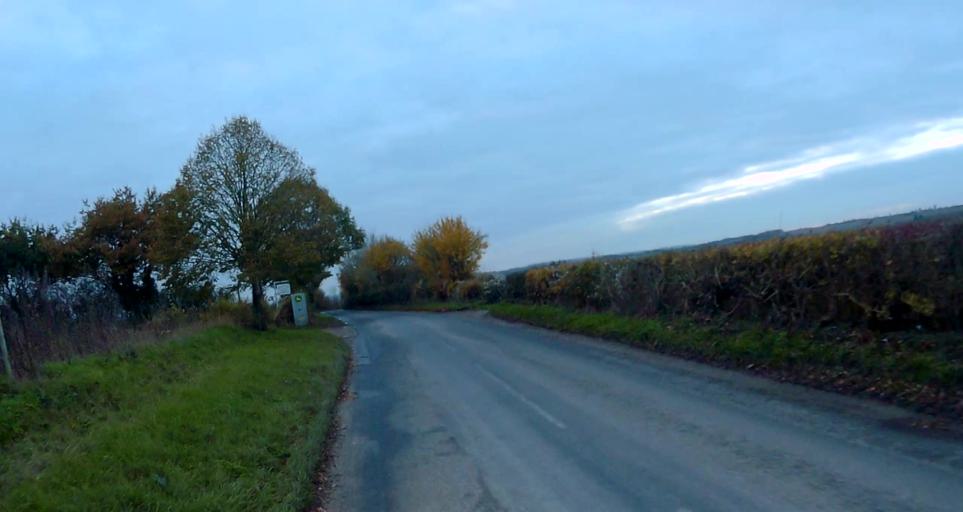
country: GB
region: England
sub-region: Hampshire
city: Odiham
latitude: 51.2511
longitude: -0.9643
